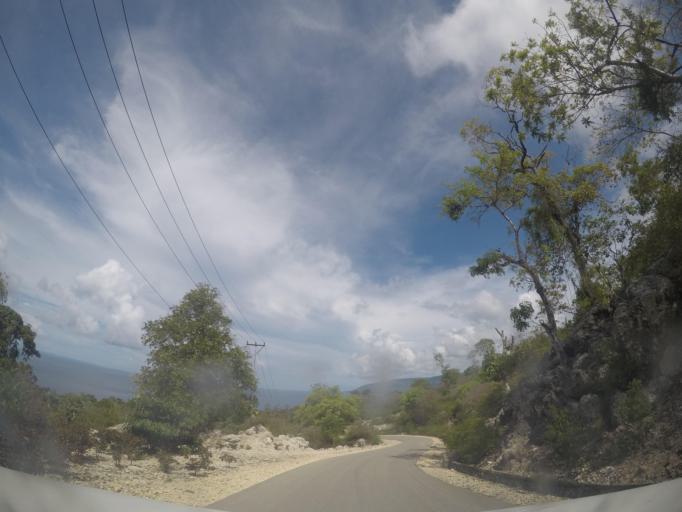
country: TL
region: Lautem
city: Lospalos
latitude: -8.3646
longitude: 127.0533
